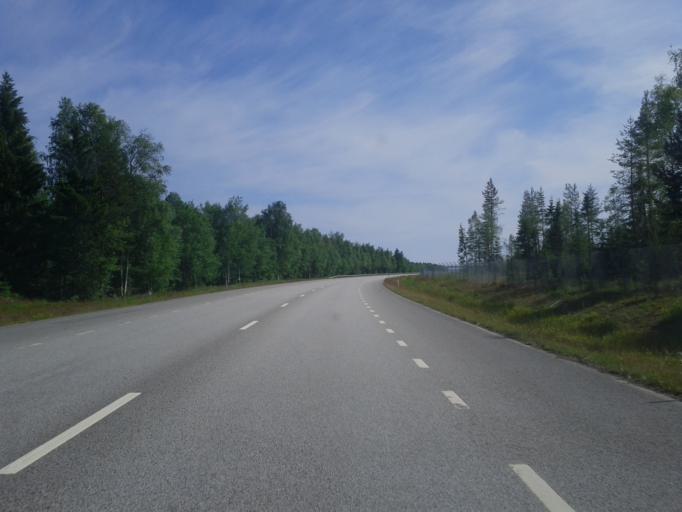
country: SE
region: Vaesterbotten
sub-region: Umea Kommun
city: Umea
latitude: 63.7868
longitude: 20.3024
